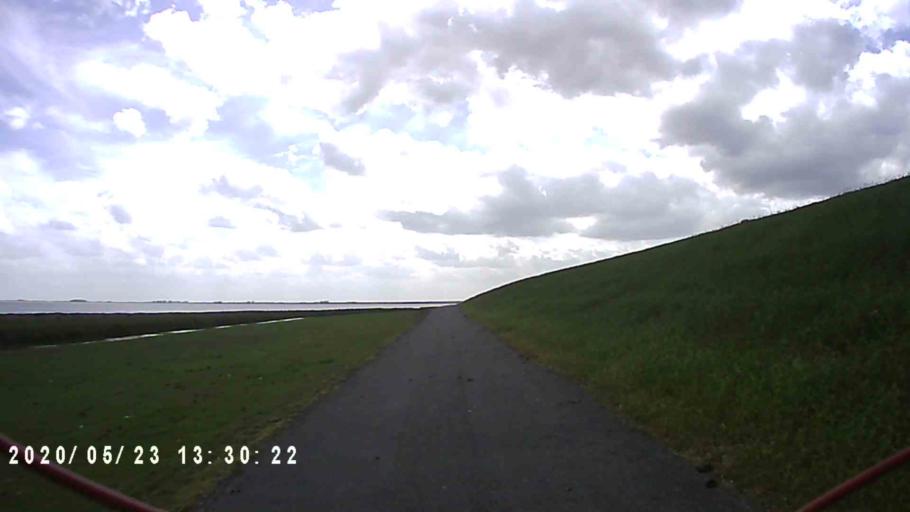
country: NL
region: Groningen
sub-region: Gemeente  Oldambt
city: Winschoten
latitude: 53.2749
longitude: 7.0789
